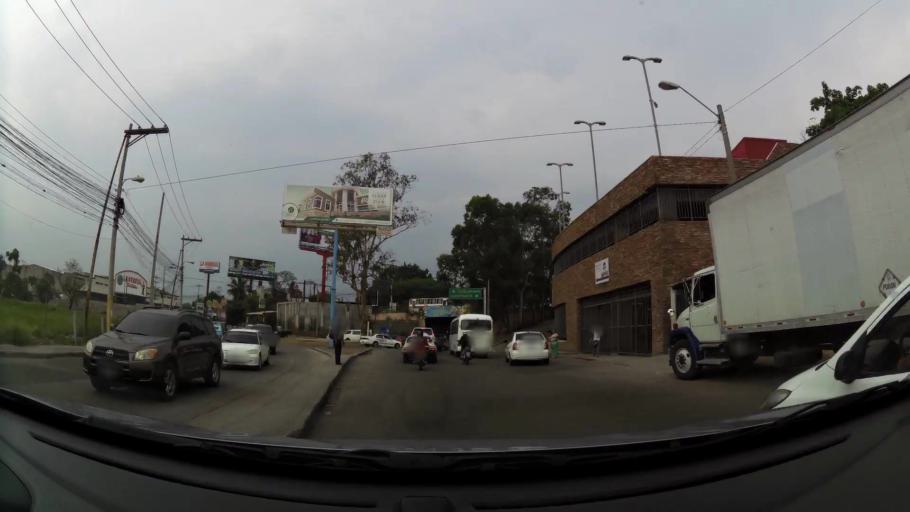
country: HN
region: Francisco Morazan
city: Tegucigalpa
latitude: 14.0640
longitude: -87.2199
